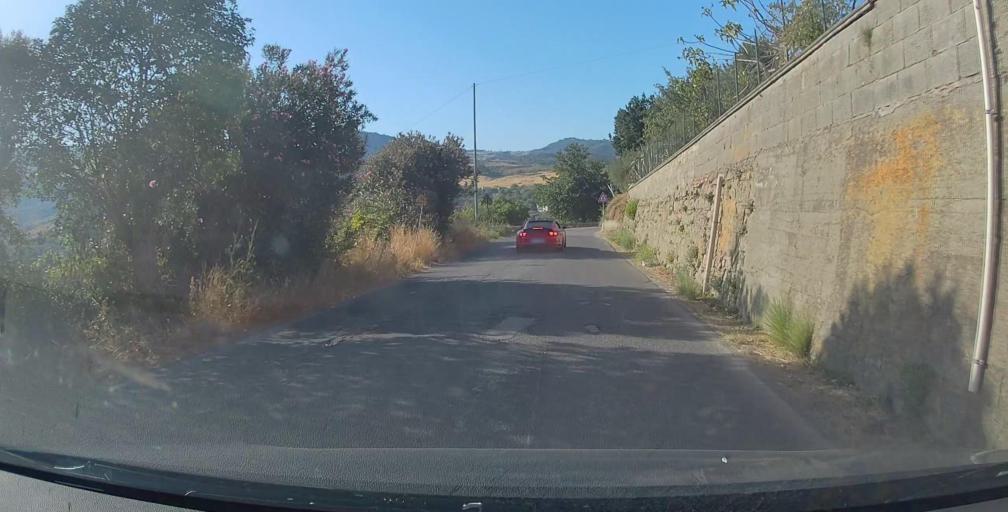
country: IT
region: Sicily
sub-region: Messina
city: Librizzi
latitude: 38.0822
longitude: 14.9743
